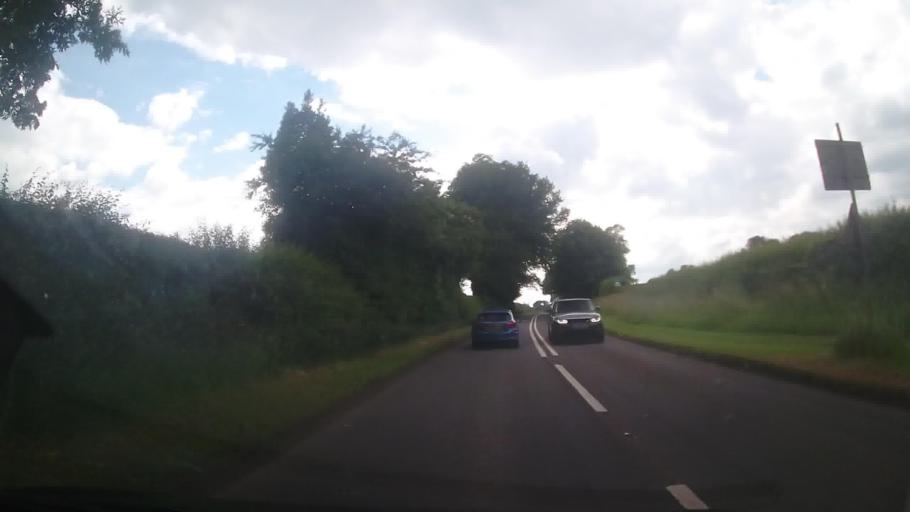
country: GB
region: England
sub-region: Shropshire
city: Ellesmere
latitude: 52.9012
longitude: -2.9123
